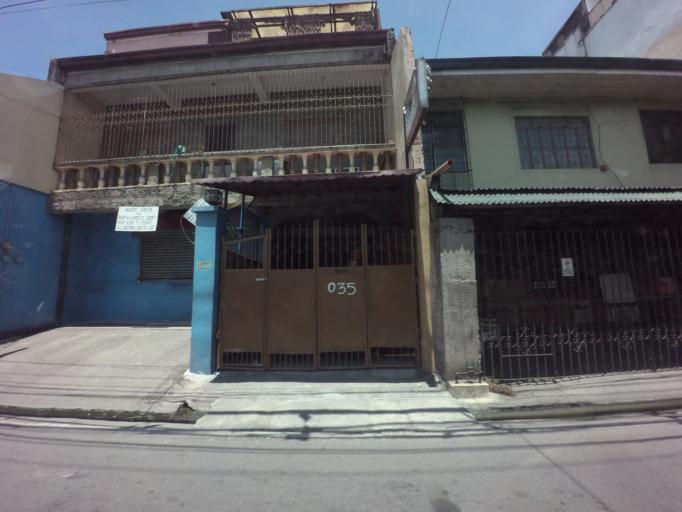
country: PH
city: Sambayanihan People's Village
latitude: 14.4838
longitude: 120.9841
